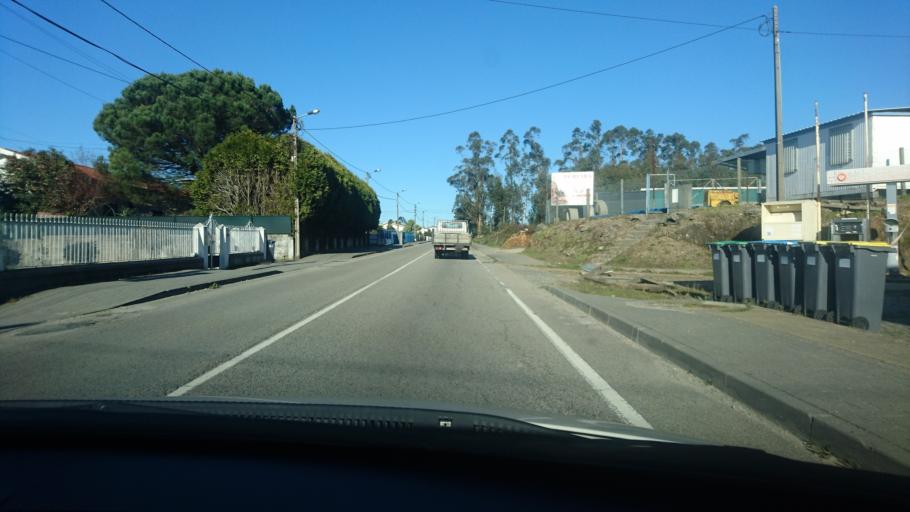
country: PT
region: Aveiro
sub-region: Santa Maria da Feira
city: Arrifana
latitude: 40.9350
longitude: -8.5053
